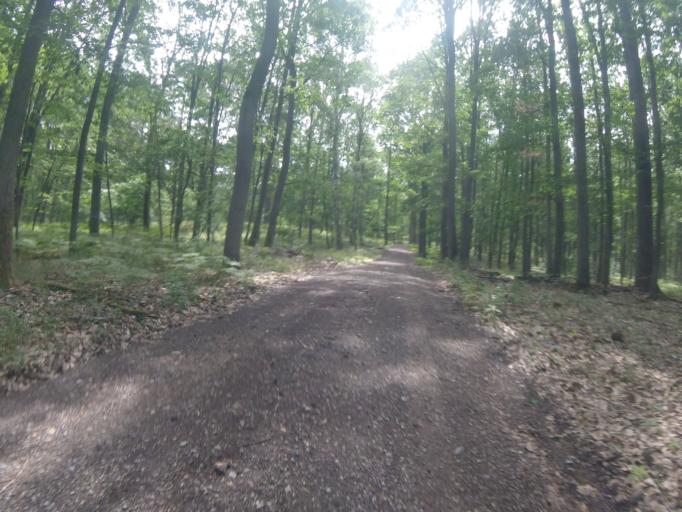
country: DE
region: Brandenburg
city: Gross Koris
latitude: 52.2007
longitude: 13.6867
